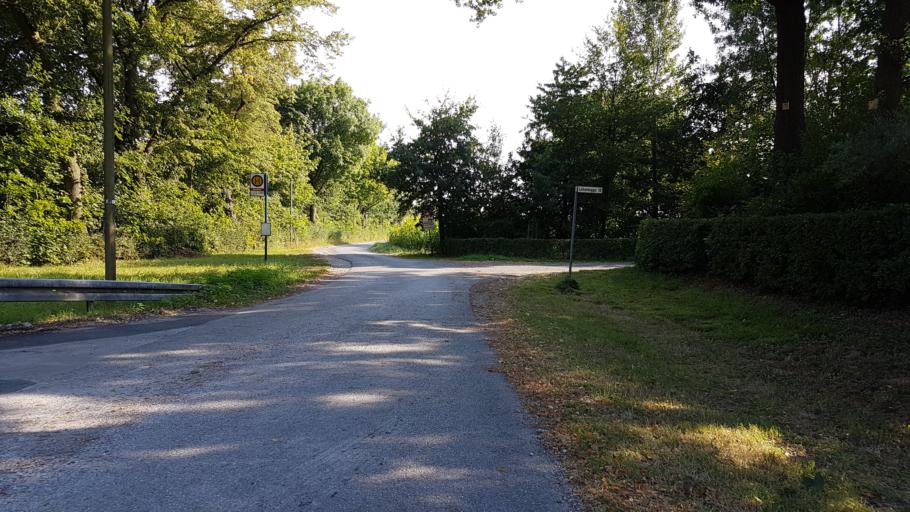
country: DE
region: North Rhine-Westphalia
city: Datteln
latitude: 51.6861
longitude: 7.3766
